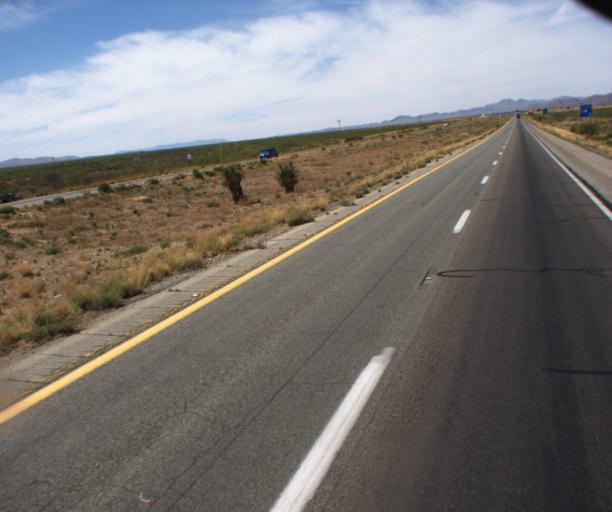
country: US
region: Arizona
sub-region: Cochise County
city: Willcox
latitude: 32.3233
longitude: -109.5028
